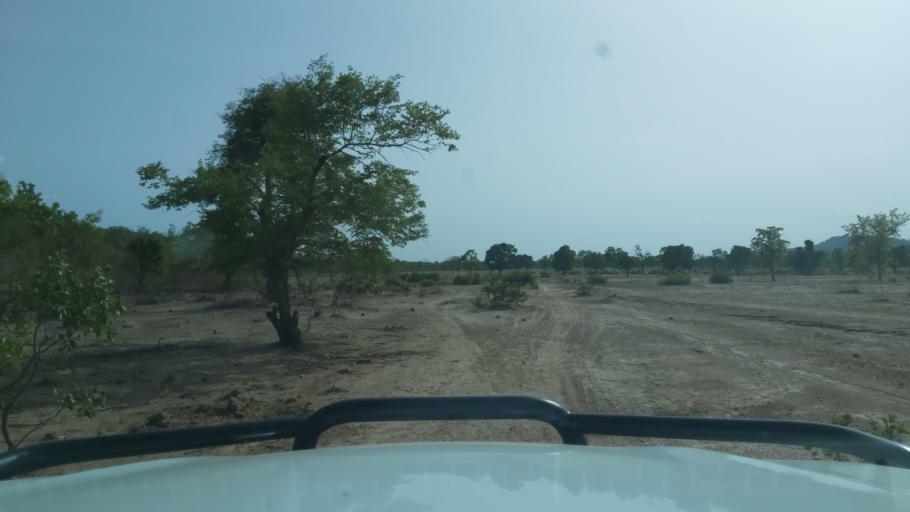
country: ML
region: Koulikoro
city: Koulikoro
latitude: 13.1756
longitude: -7.7429
